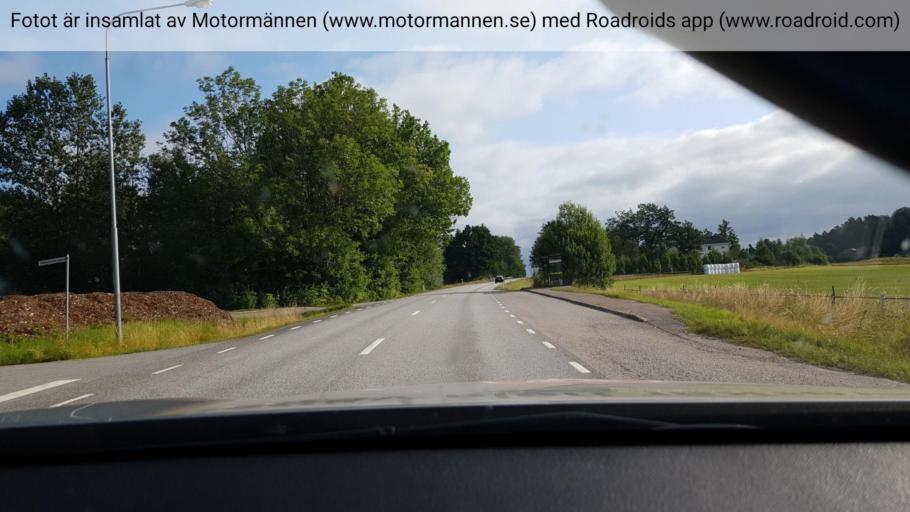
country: SE
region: Stockholm
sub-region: Norrtalje Kommun
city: Rimbo
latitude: 59.6841
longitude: 18.3667
